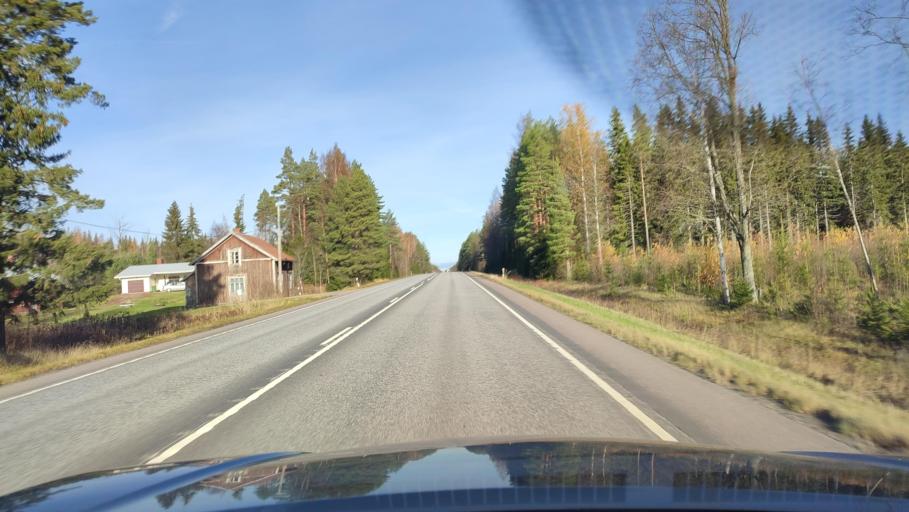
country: FI
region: Ostrobothnia
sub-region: Vaasa
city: Malax
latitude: 62.8158
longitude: 21.6852
